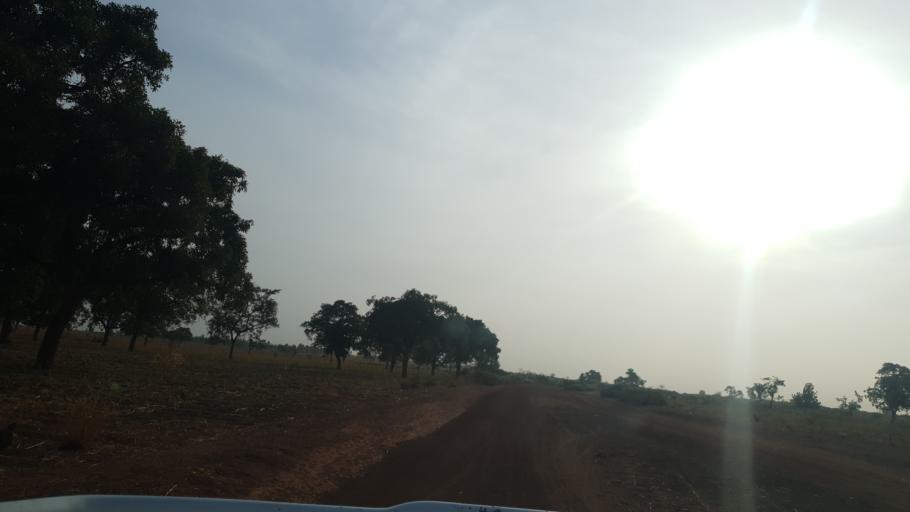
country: ML
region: Koulikoro
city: Dioila
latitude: 12.7697
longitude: -6.9269
